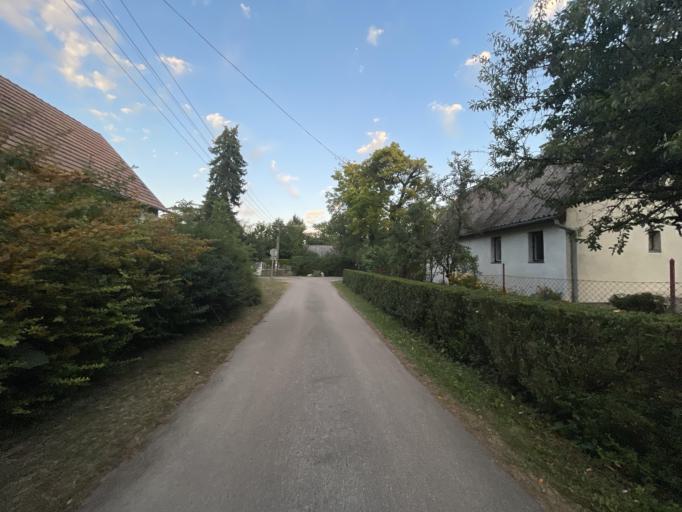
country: HU
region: Fejer
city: Lepseny
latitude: 46.9789
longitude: 18.1690
